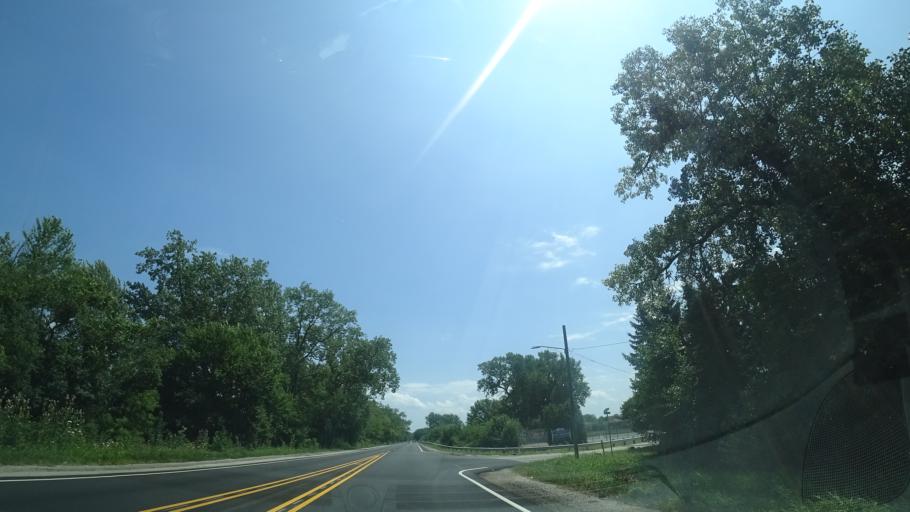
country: US
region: Illinois
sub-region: Cook County
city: Crestwood
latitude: 41.6687
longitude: -87.7686
